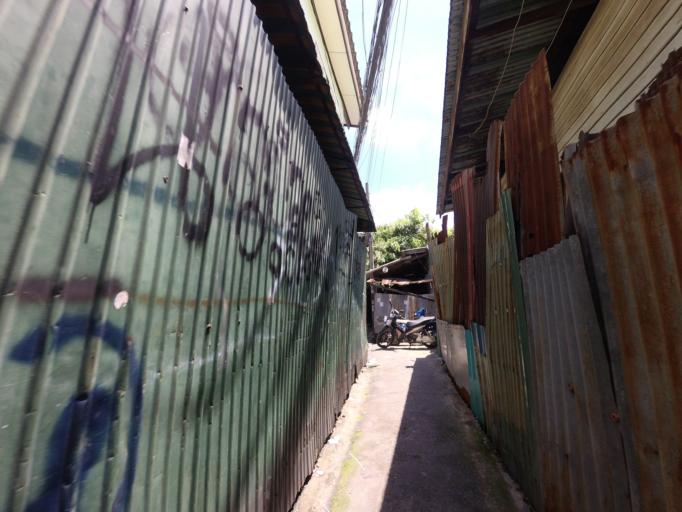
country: TH
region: Bangkok
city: Lat Phrao
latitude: 13.8021
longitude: 100.5884
